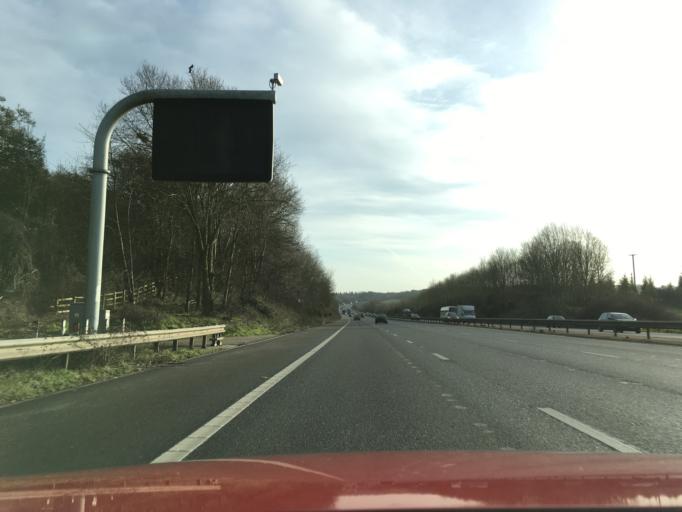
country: GB
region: England
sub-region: West Berkshire
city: Hermitage
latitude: 51.4629
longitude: -1.2378
